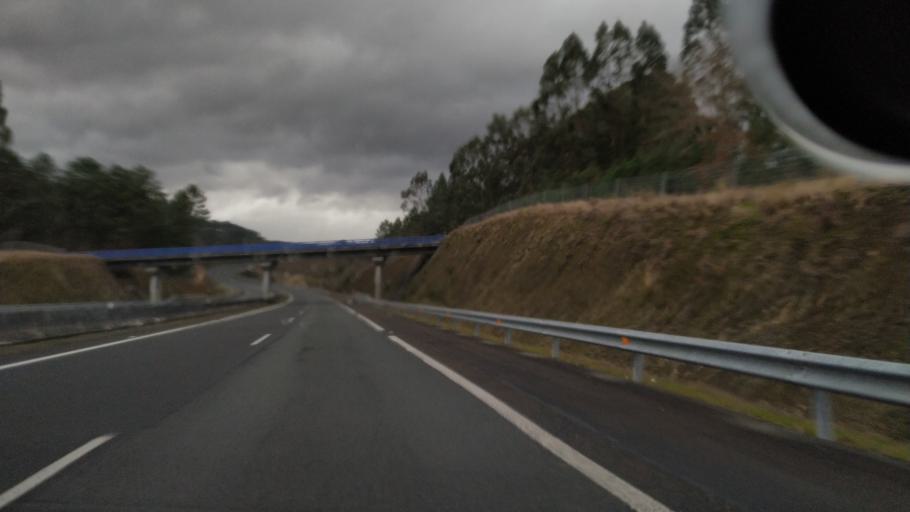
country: ES
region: Galicia
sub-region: Provincia da Coruna
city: Vedra
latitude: 42.7905
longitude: -8.4793
